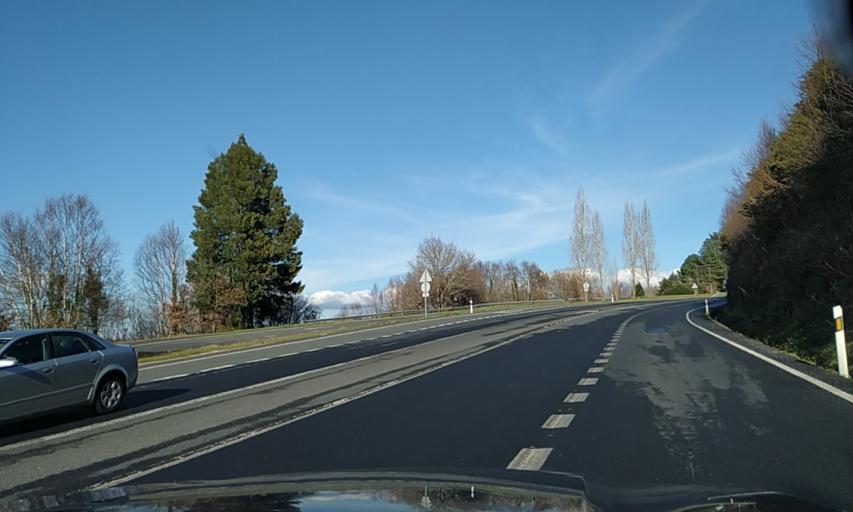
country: ES
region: Galicia
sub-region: Provincia da Coruna
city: Ribeira
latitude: 42.7128
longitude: -8.3793
